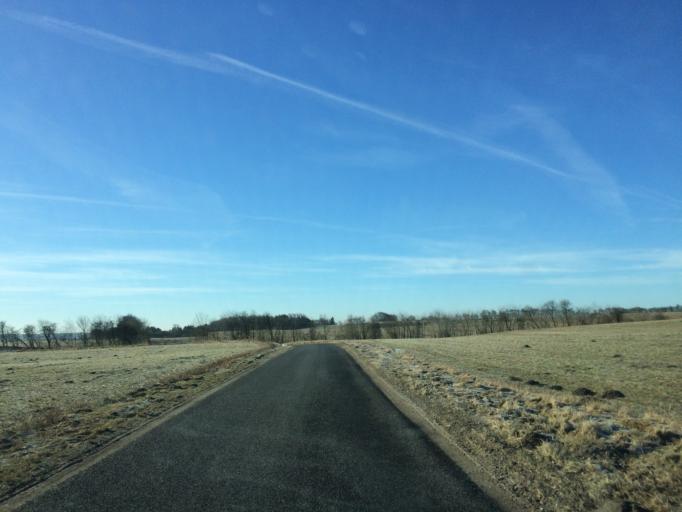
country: DK
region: North Denmark
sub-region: Mariagerfjord Kommune
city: Hobro
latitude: 56.6239
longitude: 9.6442
